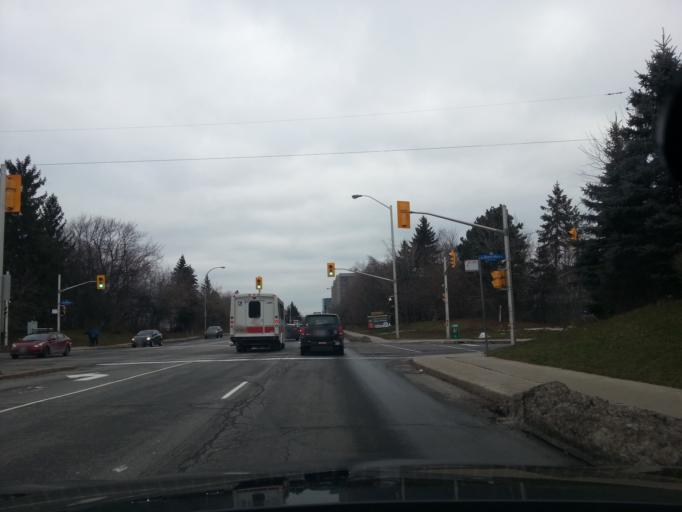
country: CA
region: Ontario
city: Ottawa
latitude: 45.4242
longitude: -75.6621
